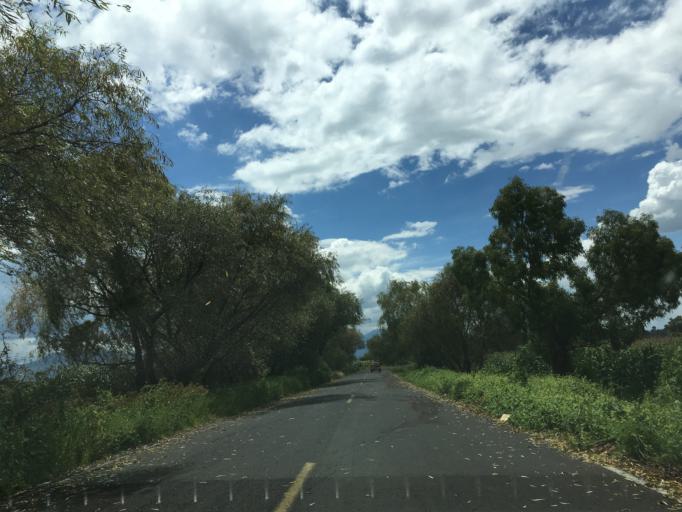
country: MX
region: Michoacan
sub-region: Zacapu
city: Naranja de Tapia
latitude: 19.8183
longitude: -101.6922
